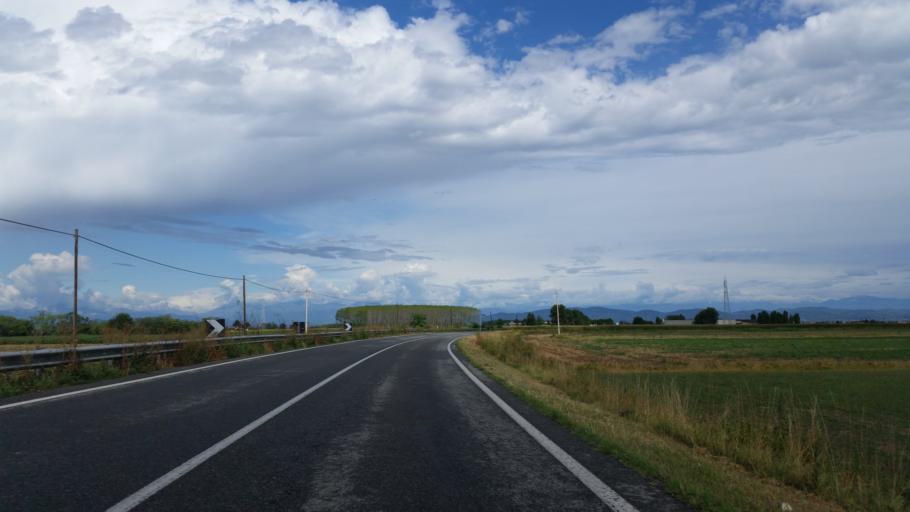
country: IT
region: Piedmont
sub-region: Provincia di Torino
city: Poirino
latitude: 44.8873
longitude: 7.8696
